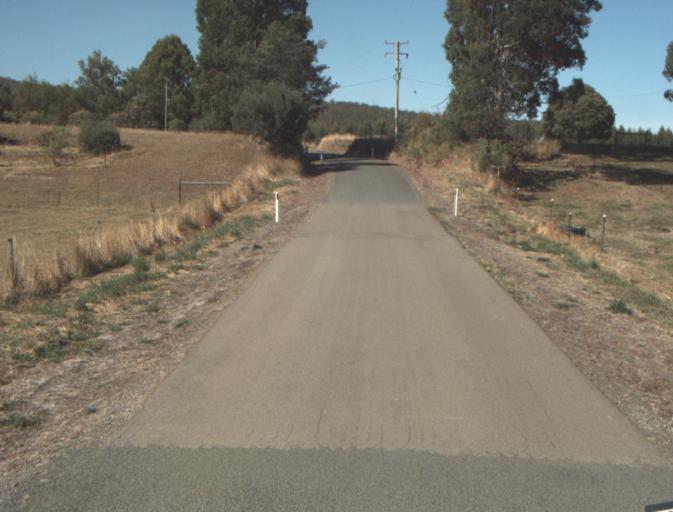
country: AU
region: Tasmania
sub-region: Launceston
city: Newstead
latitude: -41.3183
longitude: 147.3198
